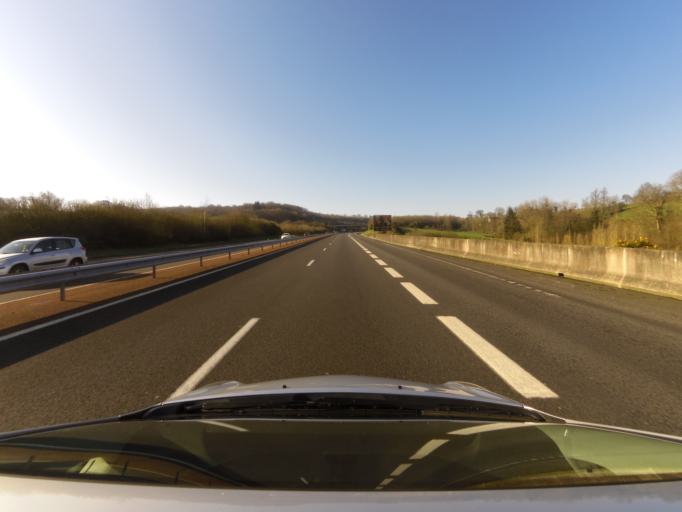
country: FR
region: Lower Normandy
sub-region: Departement de la Manche
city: Tessy-sur-Vire
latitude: 48.9305
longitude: -1.0738
